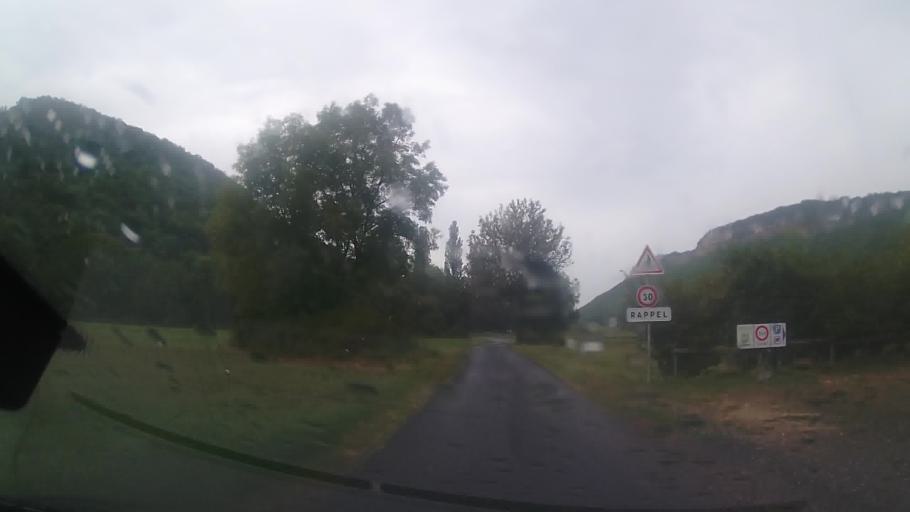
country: FR
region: Aquitaine
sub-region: Departement de la Dordogne
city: Cenac-et-Saint-Julien
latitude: 44.7980
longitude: 1.1633
